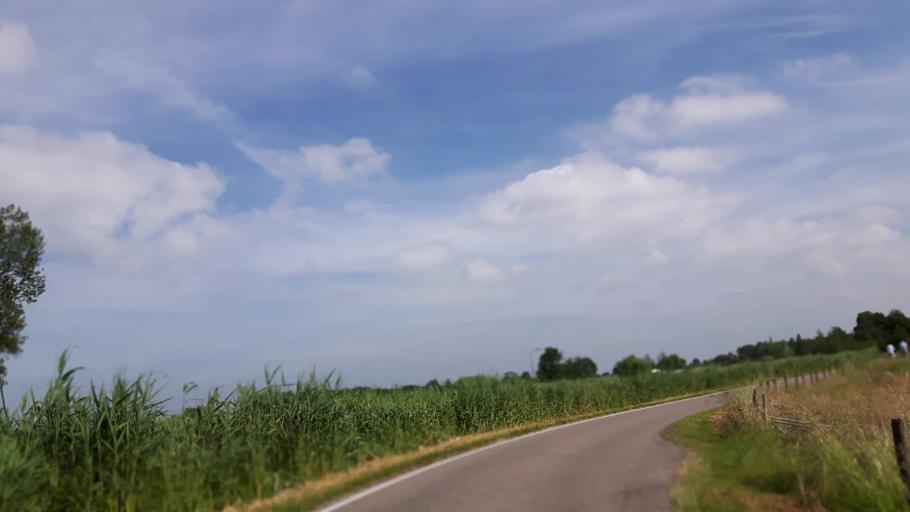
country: NL
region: Utrecht
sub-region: Gemeente De Ronde Venen
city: Mijdrecht
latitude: 52.1875
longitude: 4.8329
